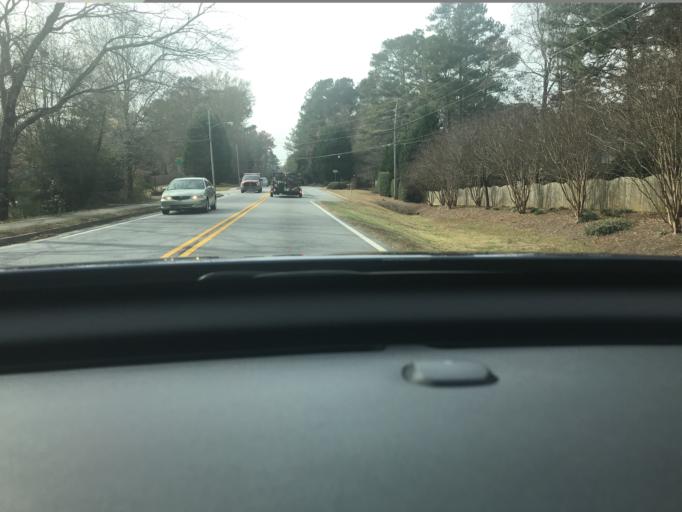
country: US
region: Georgia
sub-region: Gwinnett County
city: Mountain Park
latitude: 33.8550
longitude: -84.1055
